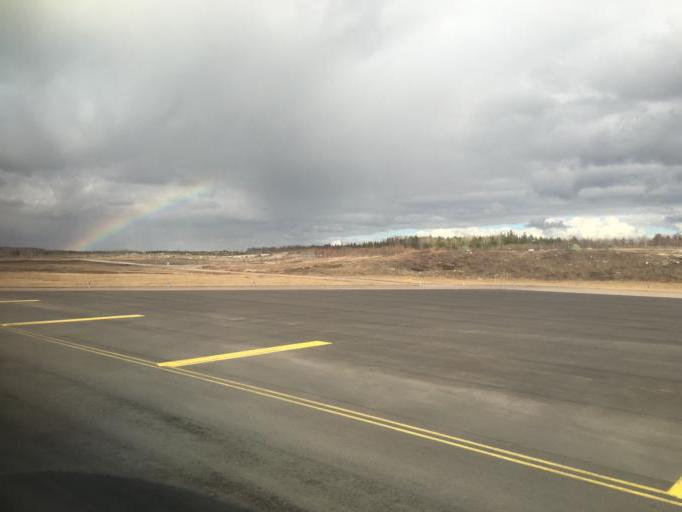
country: SE
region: Stockholm
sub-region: Sigtuna Kommun
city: Marsta
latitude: 59.6656
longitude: 17.9259
